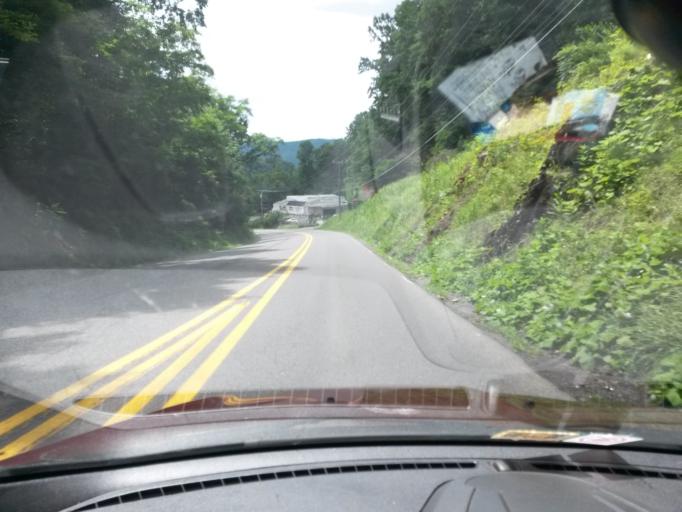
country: US
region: West Virginia
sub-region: Mercer County
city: Brush Fork
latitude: 37.2685
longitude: -81.2438
